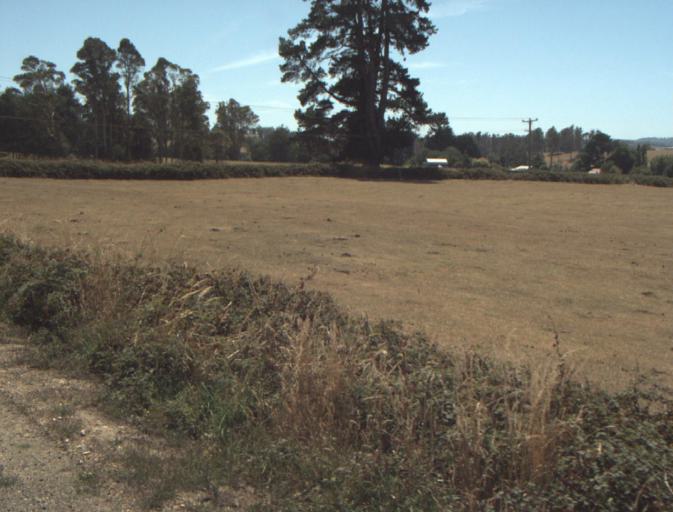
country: AU
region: Tasmania
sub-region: Launceston
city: Mayfield
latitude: -41.2673
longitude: 147.1323
